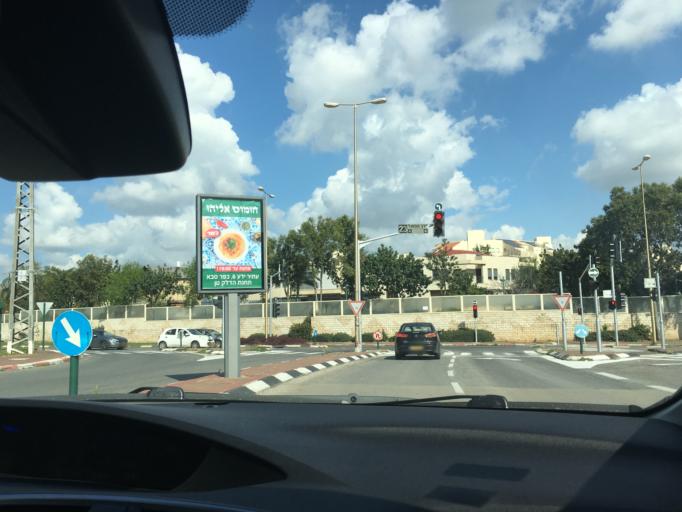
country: IL
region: Central District
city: Kfar Saba
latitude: 32.1787
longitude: 34.9283
